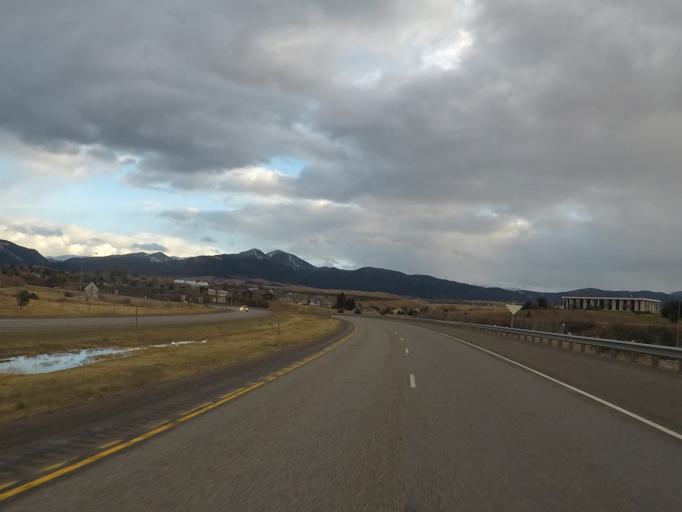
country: US
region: Montana
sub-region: Gallatin County
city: Bozeman
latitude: 45.6775
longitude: -111.0119
